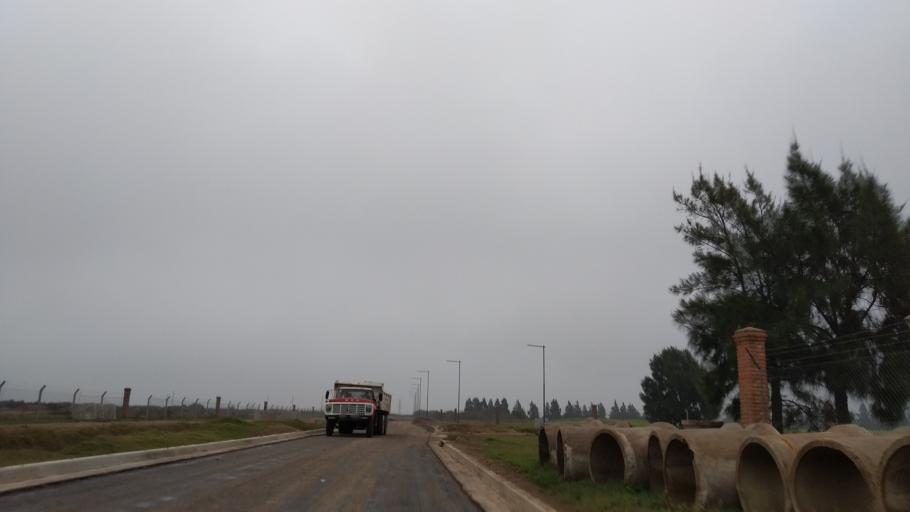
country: AR
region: Santa Fe
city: Funes
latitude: -32.9424
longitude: -60.7698
